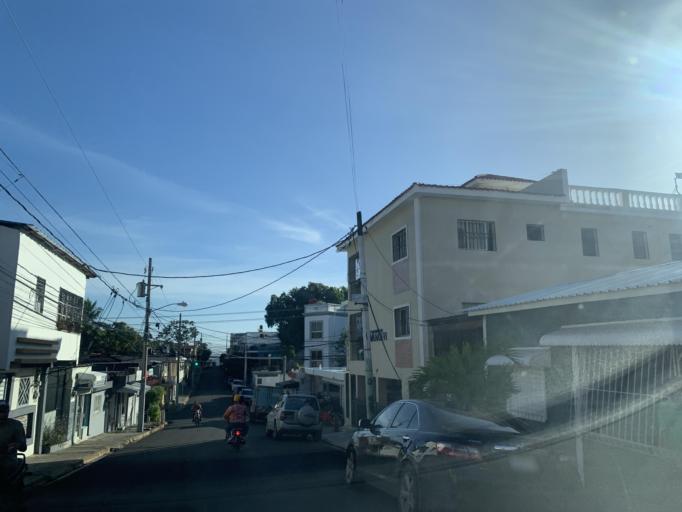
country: DO
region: Puerto Plata
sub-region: Puerto Plata
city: Puerto Plata
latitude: 19.7943
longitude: -70.6905
